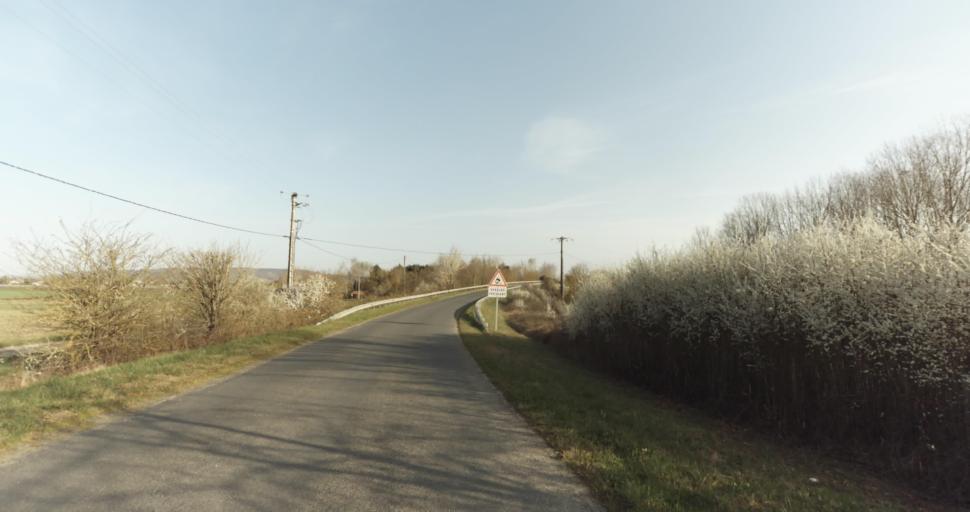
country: FR
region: Midi-Pyrenees
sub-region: Departement du Tarn
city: Saint-Sulpice-la-Pointe
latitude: 43.7515
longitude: 1.6861
